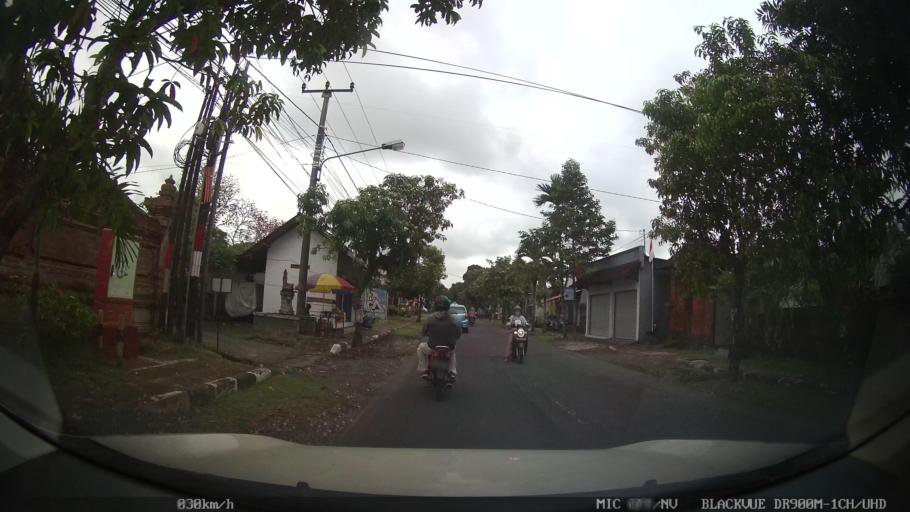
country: ID
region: Bali
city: Banjar Mambalkajanan
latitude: -8.5552
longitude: 115.2190
